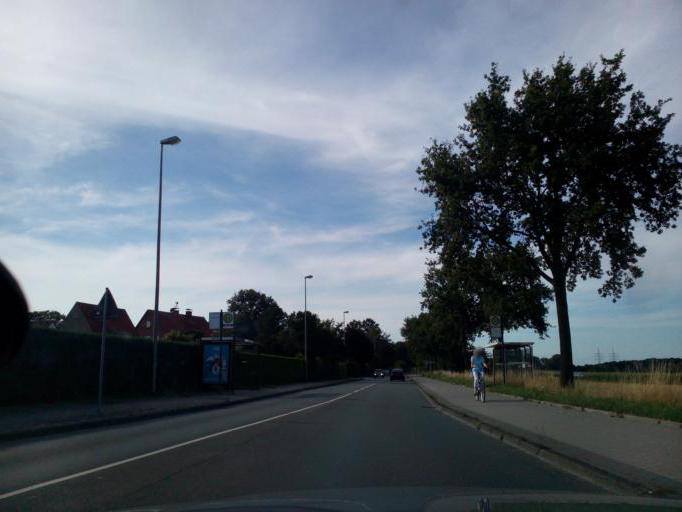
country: DE
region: North Rhine-Westphalia
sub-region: Regierungsbezirk Munster
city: Muenster
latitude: 51.9372
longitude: 7.5743
